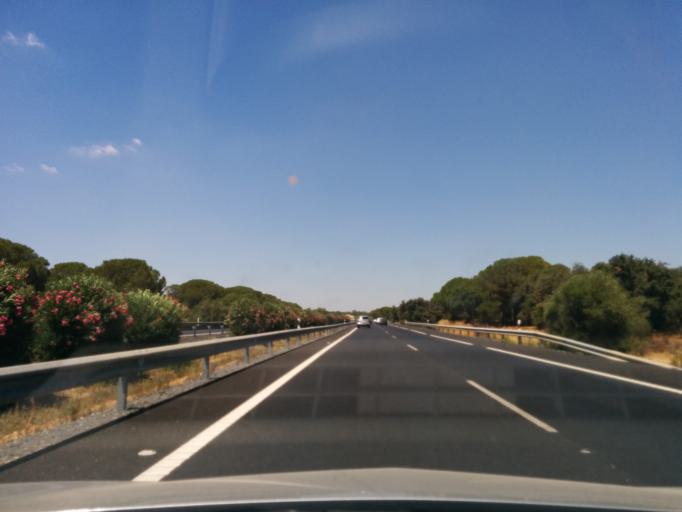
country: ES
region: Andalusia
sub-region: Provincia de Huelva
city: Manzanilla
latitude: 37.3470
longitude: -6.4598
